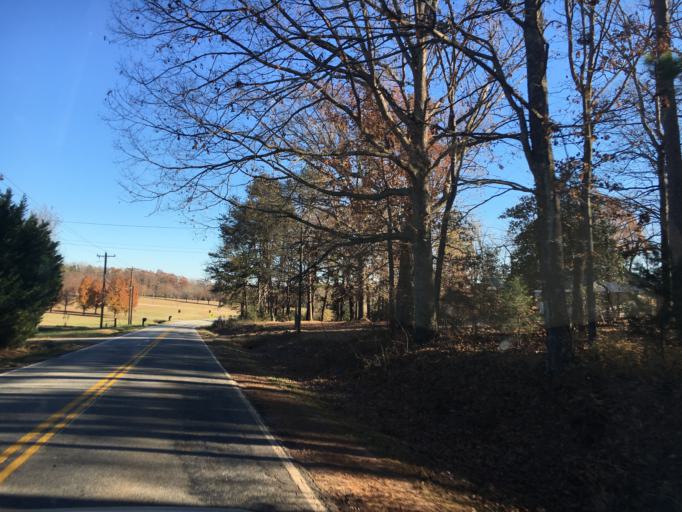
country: US
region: South Carolina
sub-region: Spartanburg County
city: Duncan
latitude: 34.9836
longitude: -82.1676
